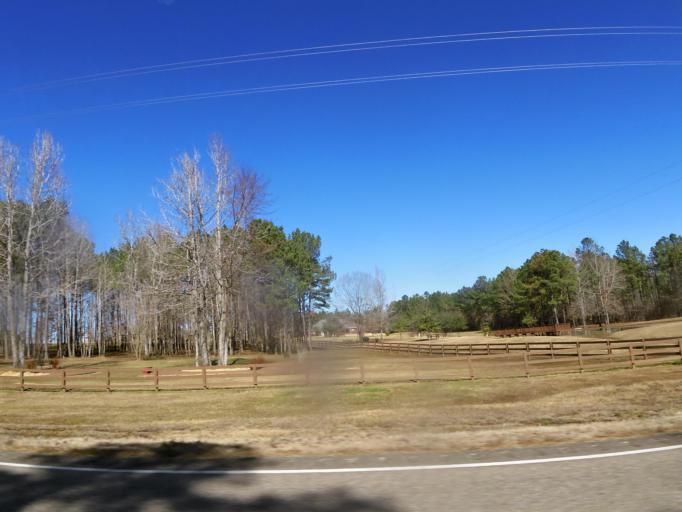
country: US
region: Alabama
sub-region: Montgomery County
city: Pike Road
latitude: 32.1851
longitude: -86.0976
